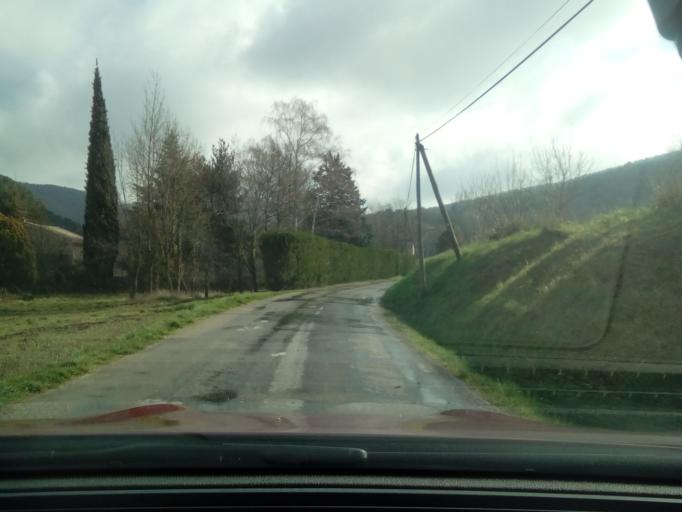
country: FR
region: Rhone-Alpes
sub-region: Departement de la Drome
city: Saulce-sur-Rhone
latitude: 44.7022
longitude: 4.8486
